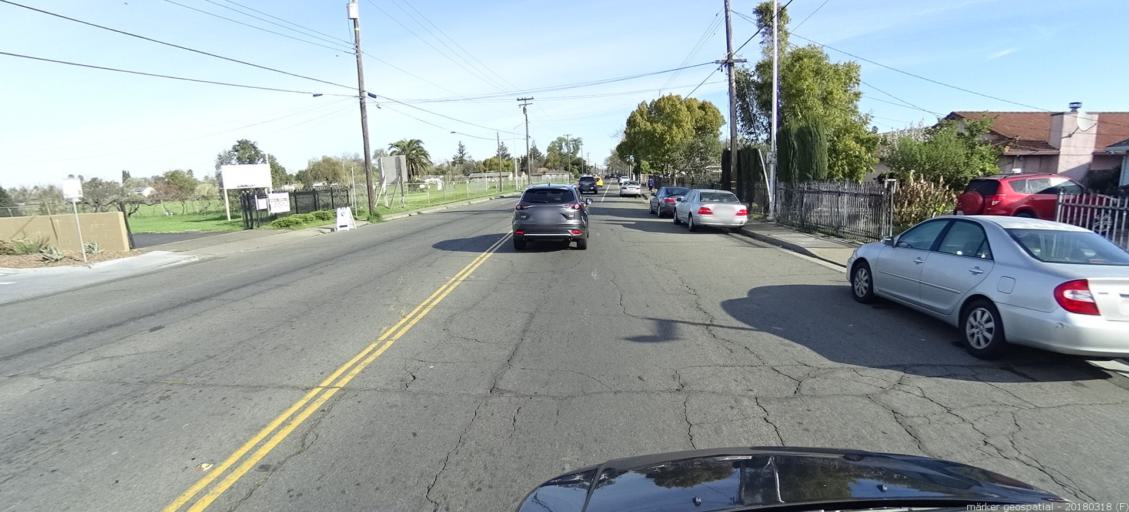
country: US
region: California
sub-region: Sacramento County
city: Parkway
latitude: 38.5257
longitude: -121.4646
